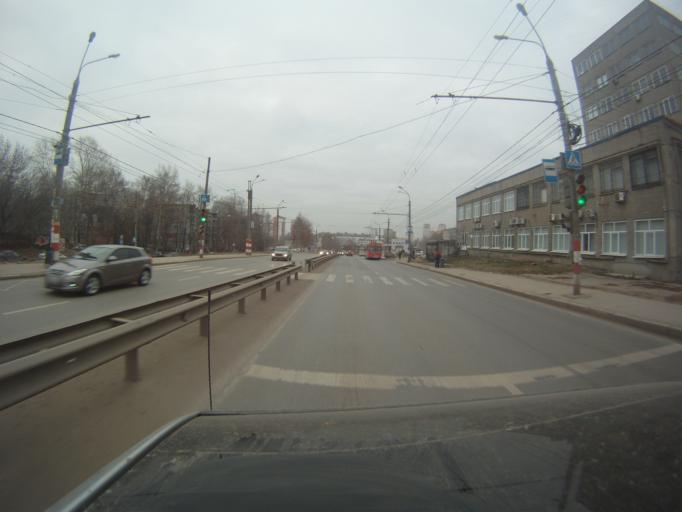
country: RU
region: Nizjnij Novgorod
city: Nizhniy Novgorod
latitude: 56.2923
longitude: 44.0356
